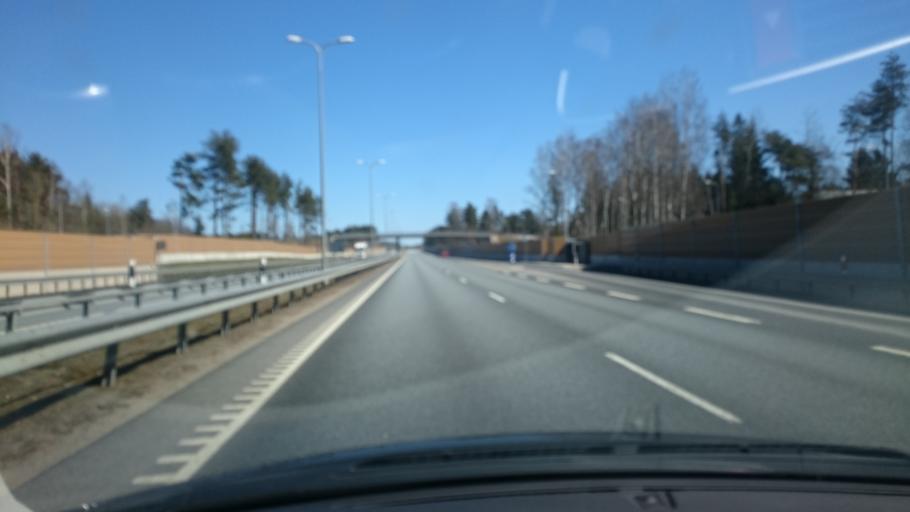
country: EE
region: Harju
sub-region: Kiili vald
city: Kiili
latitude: 59.3249
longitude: 24.7741
